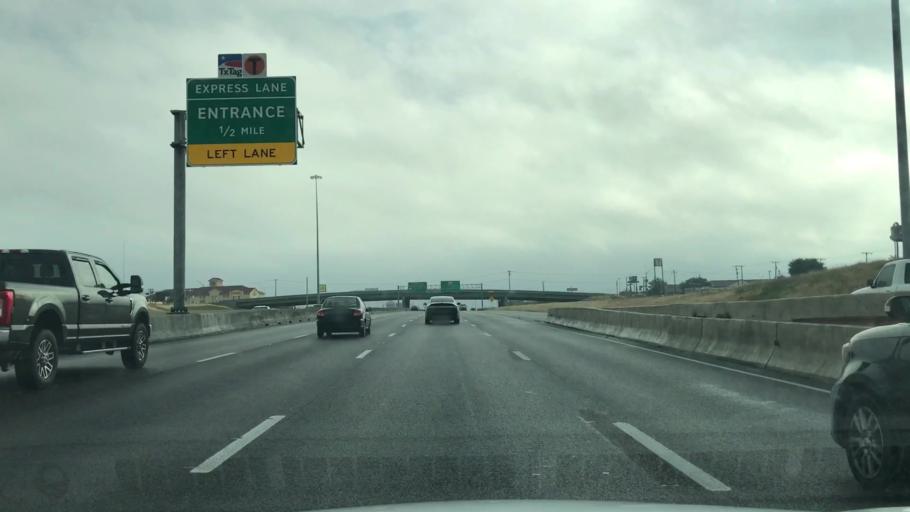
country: US
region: Texas
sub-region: Dallas County
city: Irving
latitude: 32.8368
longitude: -97.0133
